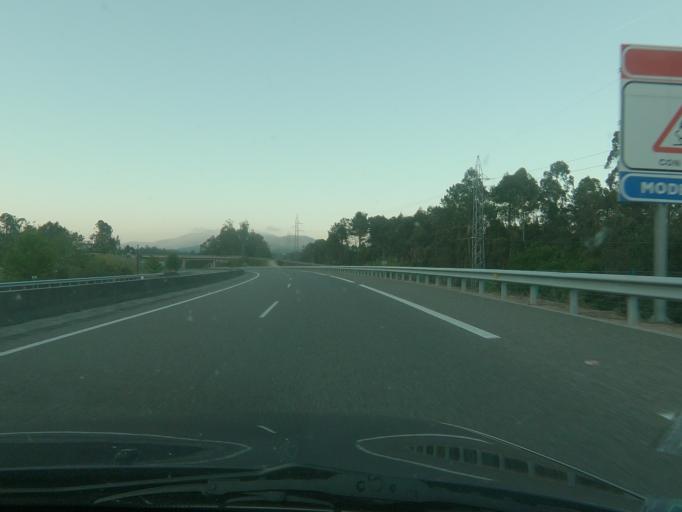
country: ES
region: Galicia
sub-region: Provincia de Pontevedra
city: Porrino
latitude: 42.1164
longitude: -8.6431
